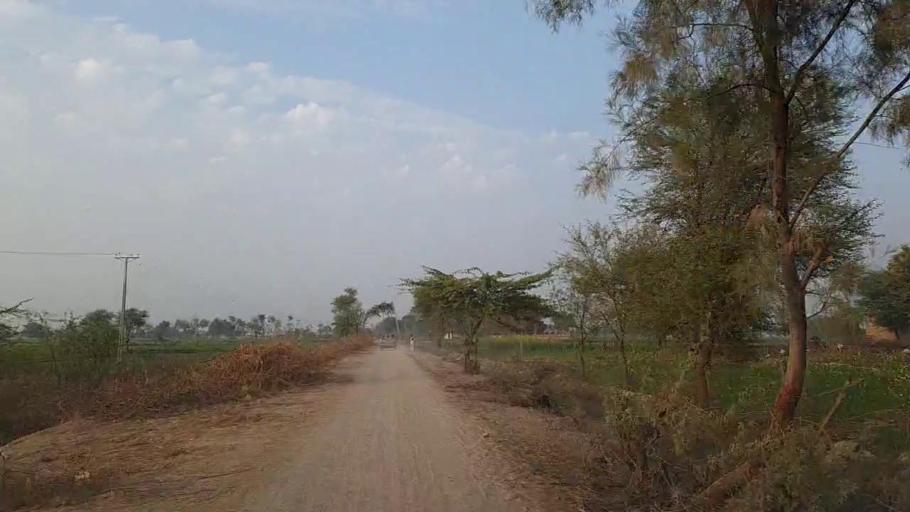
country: PK
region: Sindh
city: Jam Sahib
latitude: 26.3179
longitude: 68.6091
